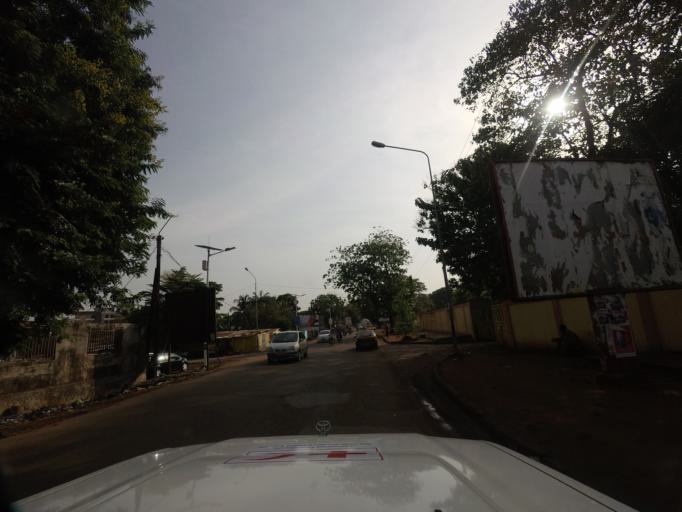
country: GN
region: Conakry
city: Conakry
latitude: 9.5451
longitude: -13.6783
